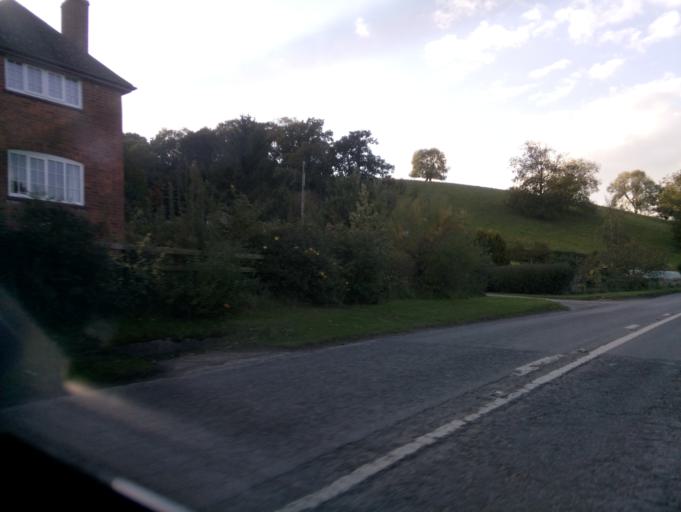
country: GB
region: England
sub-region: Herefordshire
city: Ledbury
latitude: 52.0396
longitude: -2.3963
